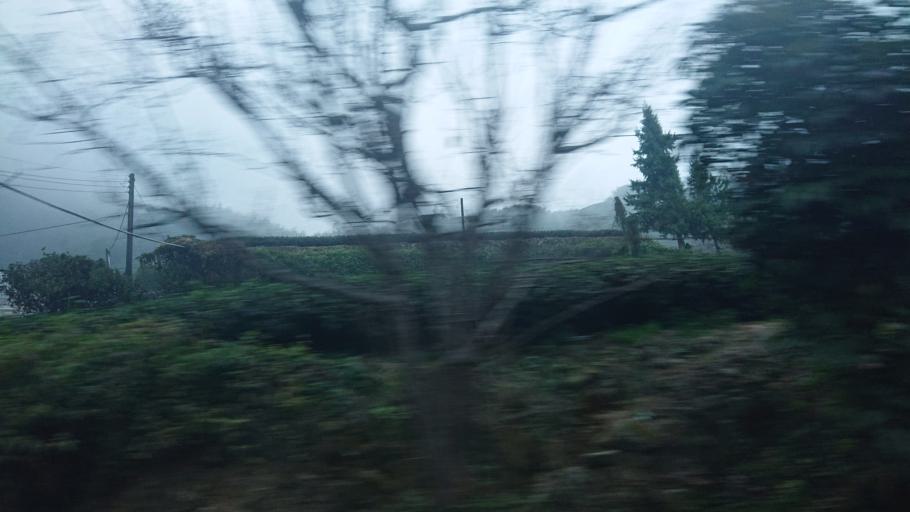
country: TW
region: Taiwan
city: Lugu
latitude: 23.5233
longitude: 120.7076
